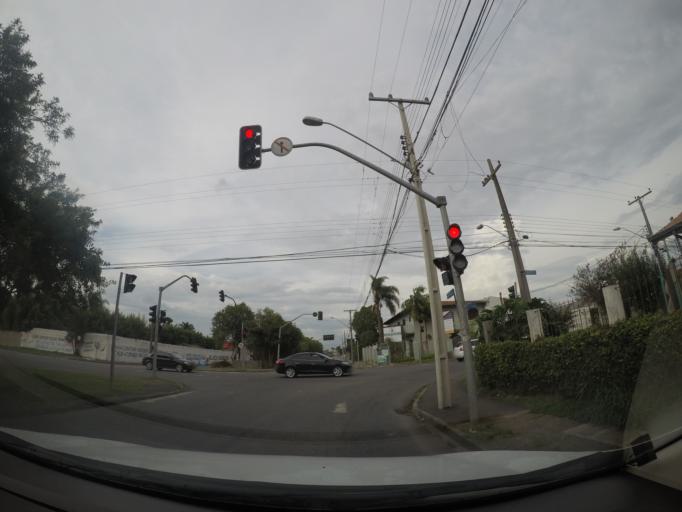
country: BR
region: Parana
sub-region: Sao Jose Dos Pinhais
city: Sao Jose dos Pinhais
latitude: -25.4963
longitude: -49.2416
